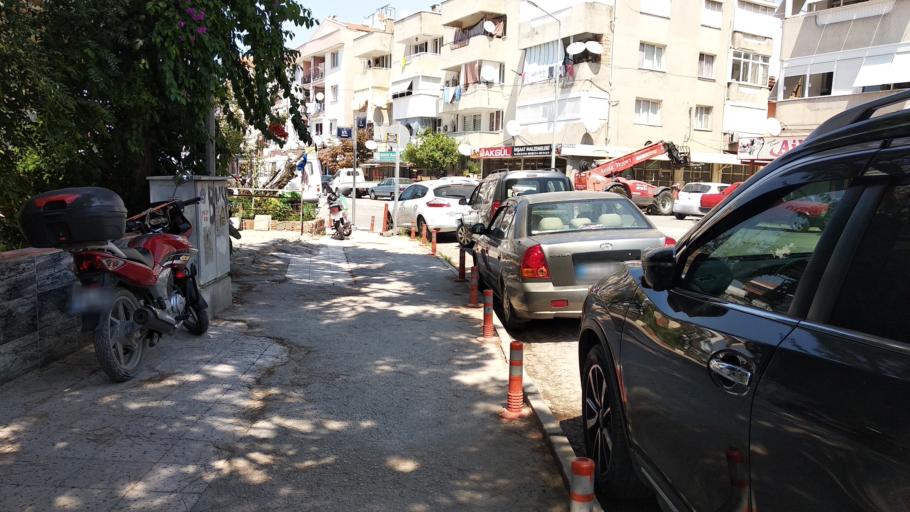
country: TR
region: Izmir
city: Dikili
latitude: 39.0739
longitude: 26.8901
